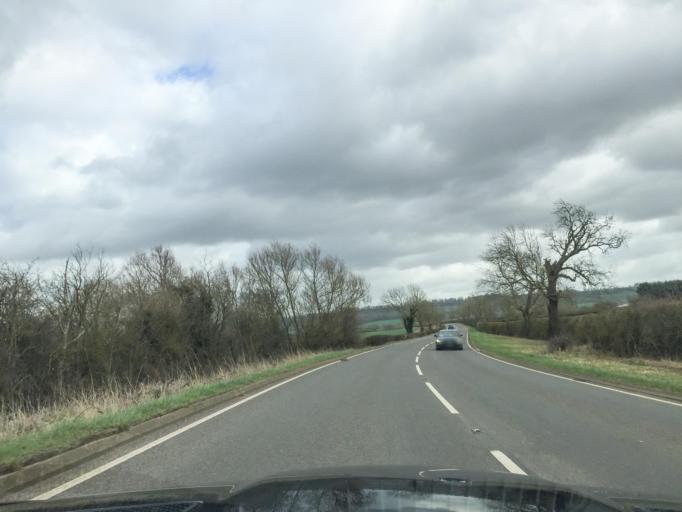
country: GB
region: England
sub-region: Warwickshire
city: Wellesbourne Mountford
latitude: 52.1222
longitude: -1.5149
